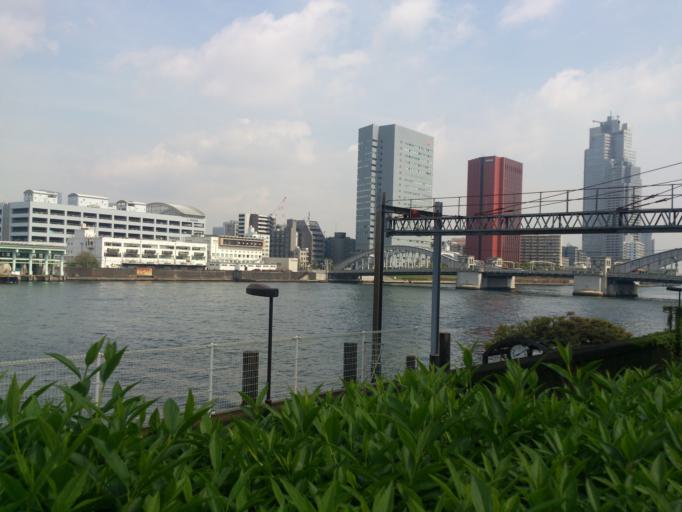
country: JP
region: Tokyo
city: Tokyo
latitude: 35.6597
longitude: 139.7734
